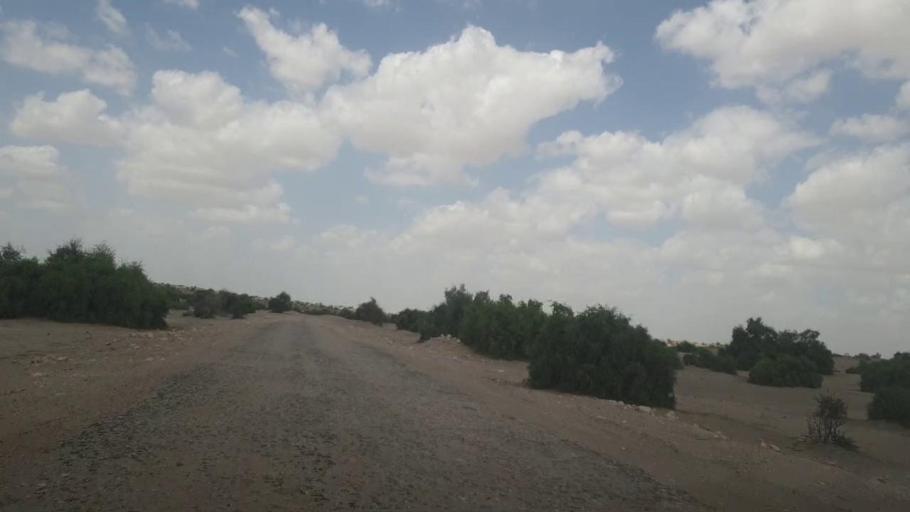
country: PK
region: Sindh
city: Kot Diji
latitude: 27.2800
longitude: 69.2247
